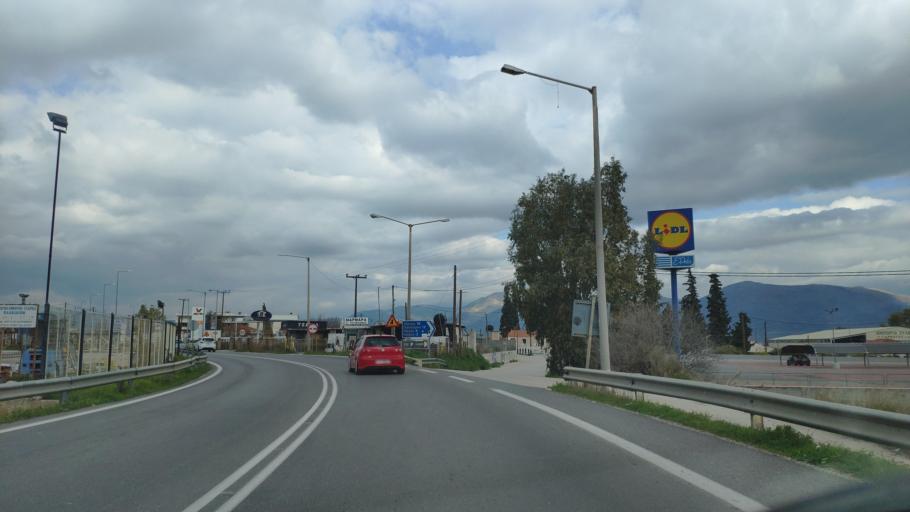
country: GR
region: Peloponnese
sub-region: Nomos Argolidos
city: Argos
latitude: 37.6473
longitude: 22.7296
